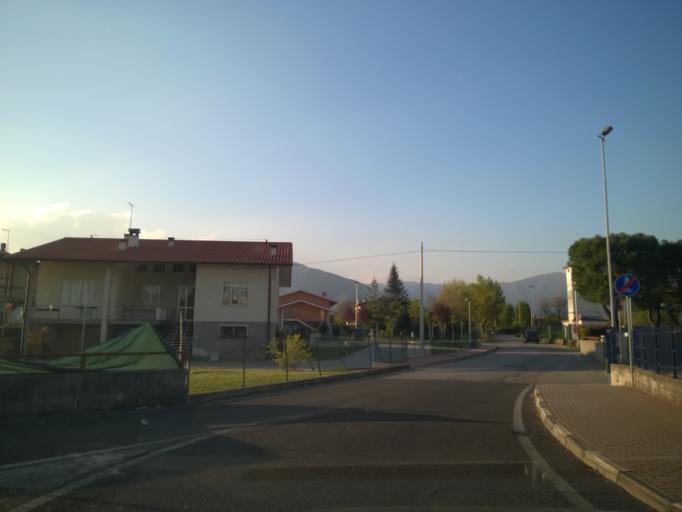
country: IT
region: Veneto
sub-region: Provincia di Vicenza
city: Marano Vicentino
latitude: 45.6983
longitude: 11.4412
